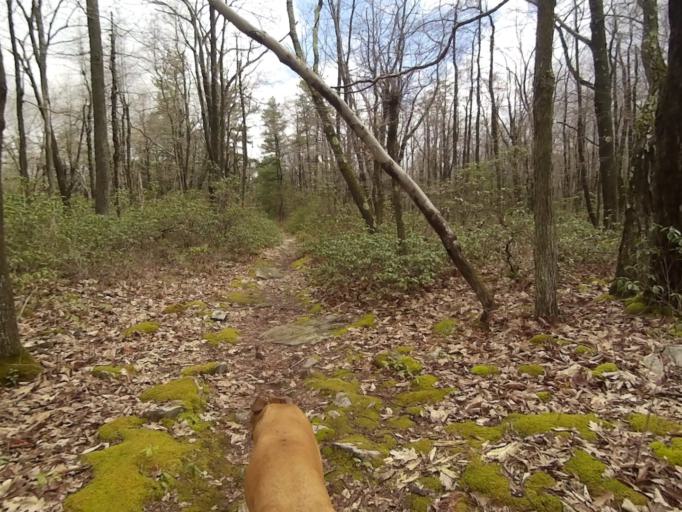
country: US
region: Pennsylvania
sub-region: Centre County
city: Boalsburg
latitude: 40.7495
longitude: -77.7550
